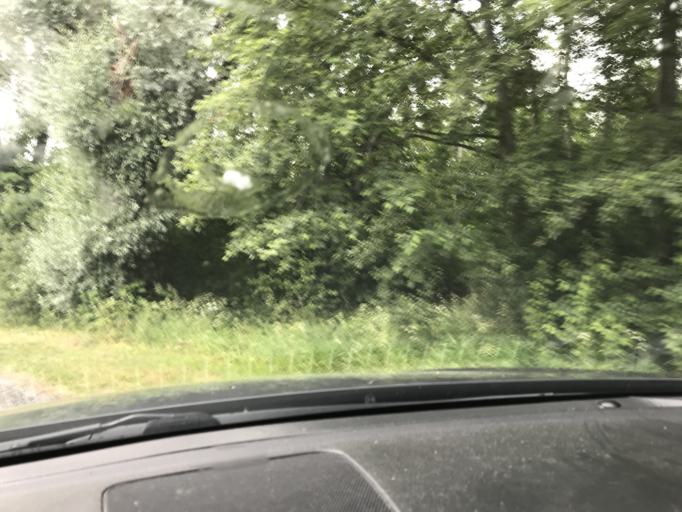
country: LV
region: Alsunga
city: Alsunga
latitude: 56.9822
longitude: 21.6337
